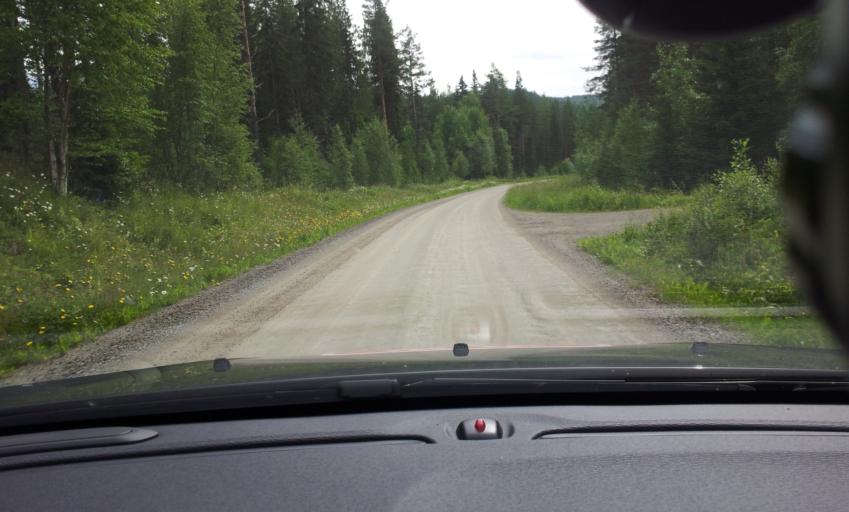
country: SE
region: Jaemtland
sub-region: OEstersunds Kommun
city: Brunflo
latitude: 62.9501
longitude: 14.9410
